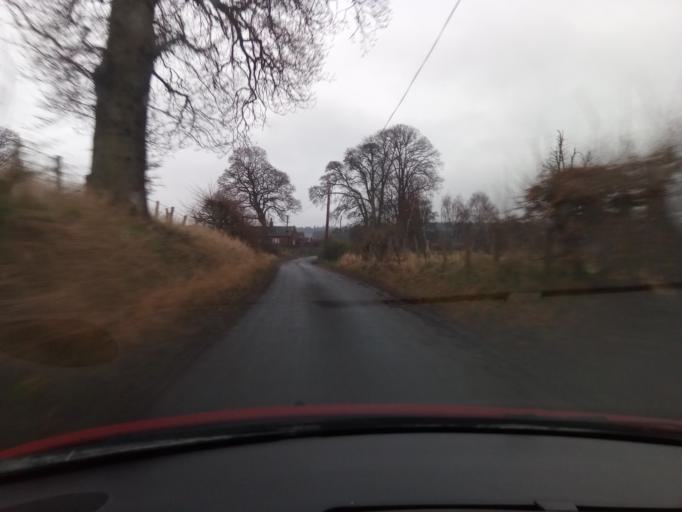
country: GB
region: Scotland
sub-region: The Scottish Borders
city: Kelso
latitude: 55.5382
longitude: -2.4457
